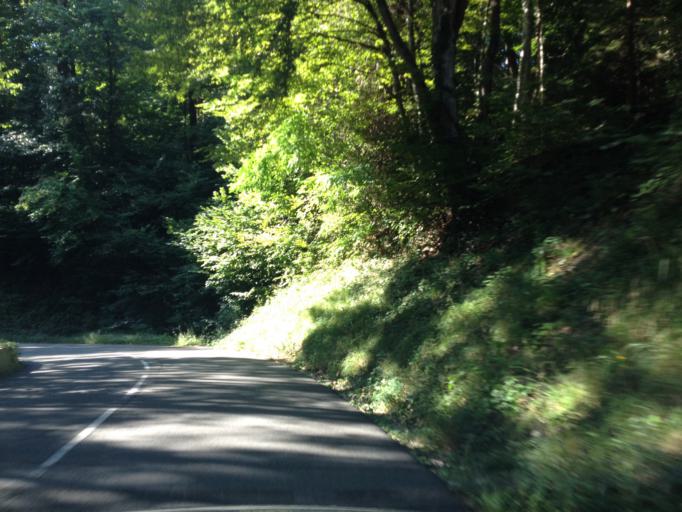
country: FR
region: Rhone-Alpes
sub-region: Departement de la Haute-Savoie
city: Cusy
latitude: 45.7229
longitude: 5.9980
